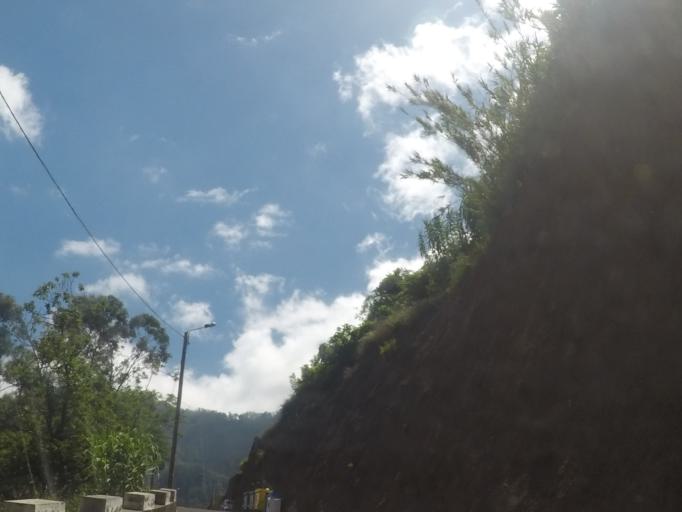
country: PT
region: Madeira
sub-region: Camara de Lobos
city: Curral das Freiras
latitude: 32.7159
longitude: -16.9709
